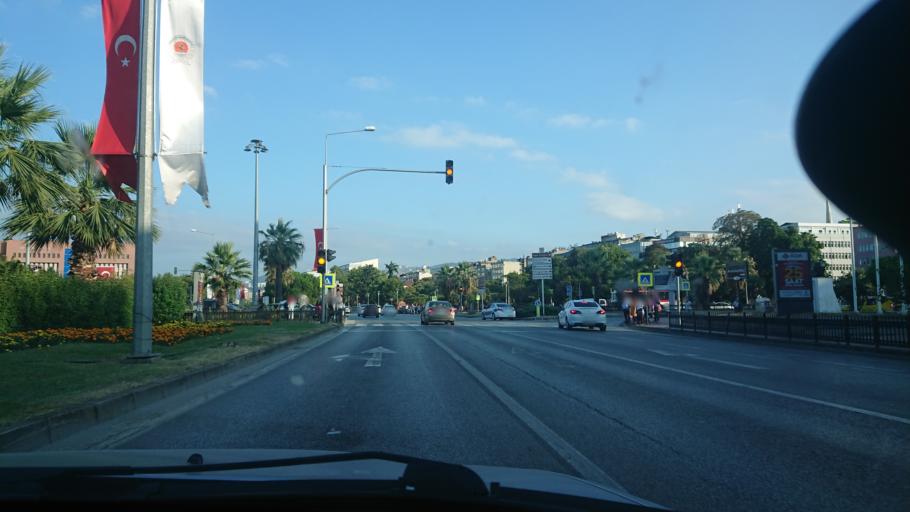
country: TR
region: Samsun
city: Samsun
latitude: 41.2913
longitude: 36.3355
